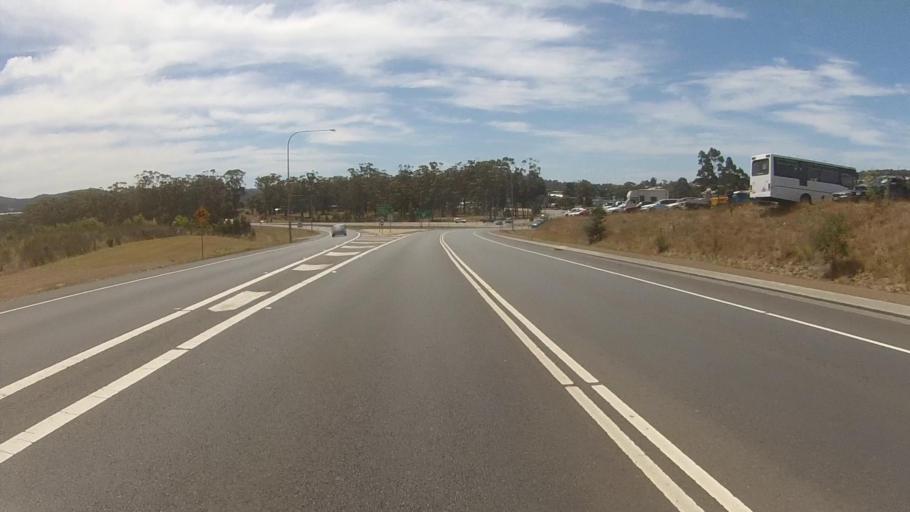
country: AU
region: Tasmania
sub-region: Kingborough
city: Kingston
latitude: -42.9882
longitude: 147.2873
